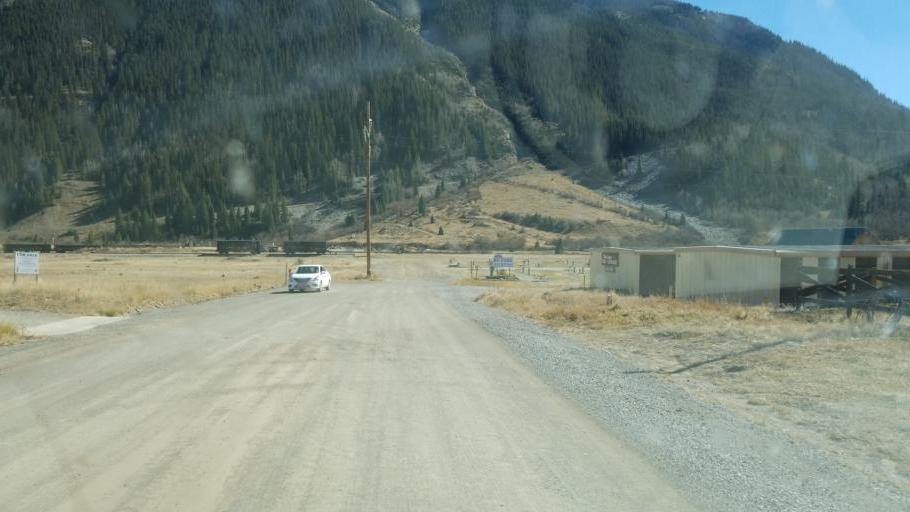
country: US
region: Colorado
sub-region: San Juan County
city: Silverton
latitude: 37.8067
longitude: -107.6672
